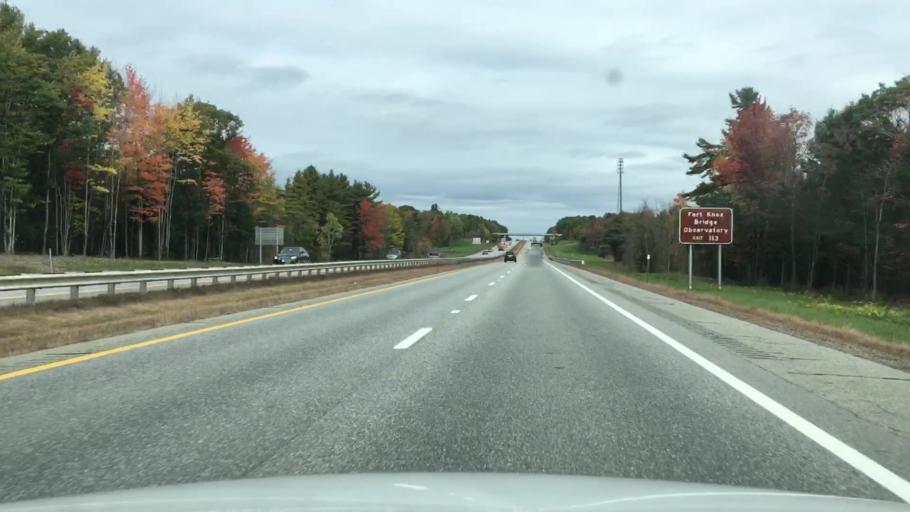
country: US
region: Maine
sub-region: Kennebec County
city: Hallowell
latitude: 44.2567
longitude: -69.8070
